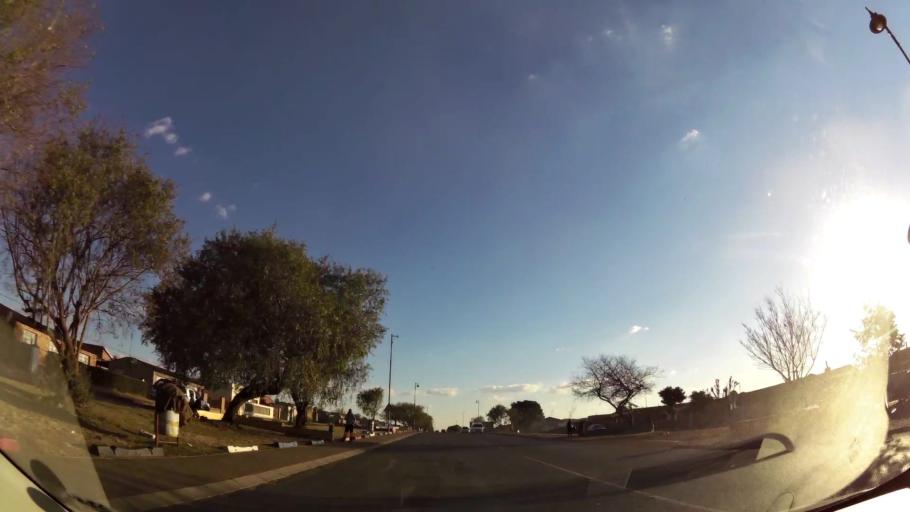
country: ZA
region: Mpumalanga
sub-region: Nkangala District Municipality
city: Witbank
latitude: -25.8789
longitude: 29.1947
